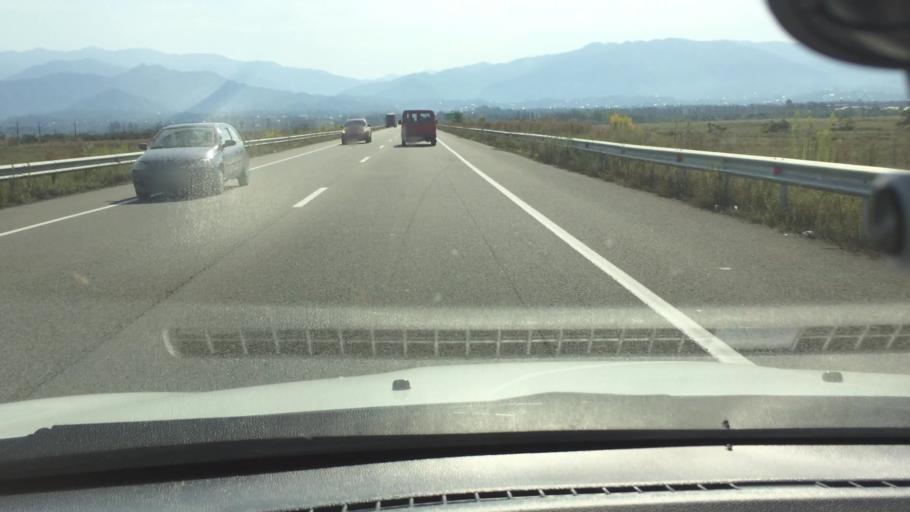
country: GE
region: Ajaria
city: Ochkhamuri
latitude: 41.8732
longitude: 41.8285
